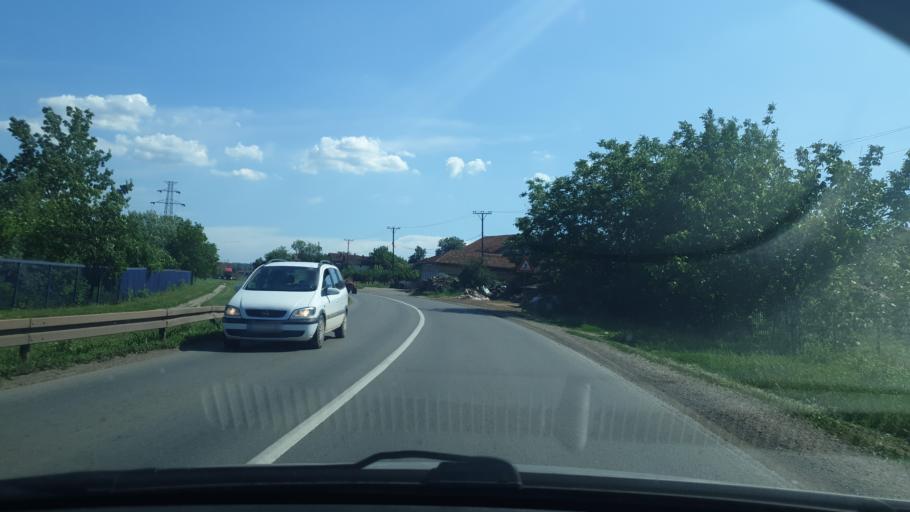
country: RS
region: Central Serbia
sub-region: Podunavski Okrug
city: Smederevo
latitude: 44.6229
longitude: 20.9611
